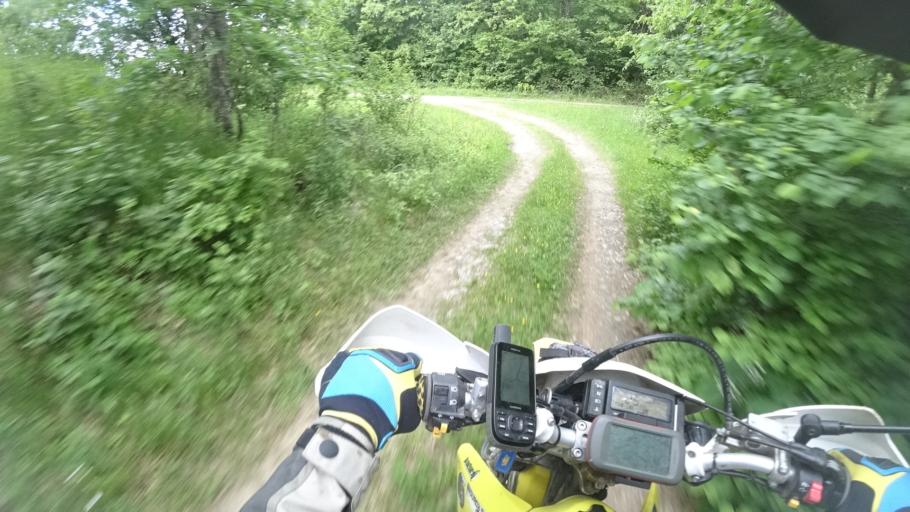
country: HR
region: Zadarska
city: Obrovac
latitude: 44.3445
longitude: 15.6526
